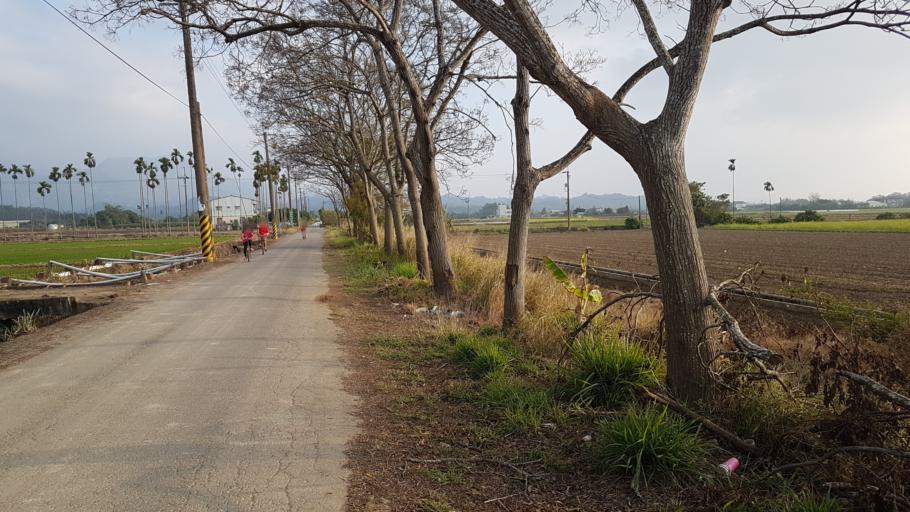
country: TW
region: Taiwan
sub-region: Chiayi
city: Jiayi Shi
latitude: 23.3757
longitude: 120.4533
